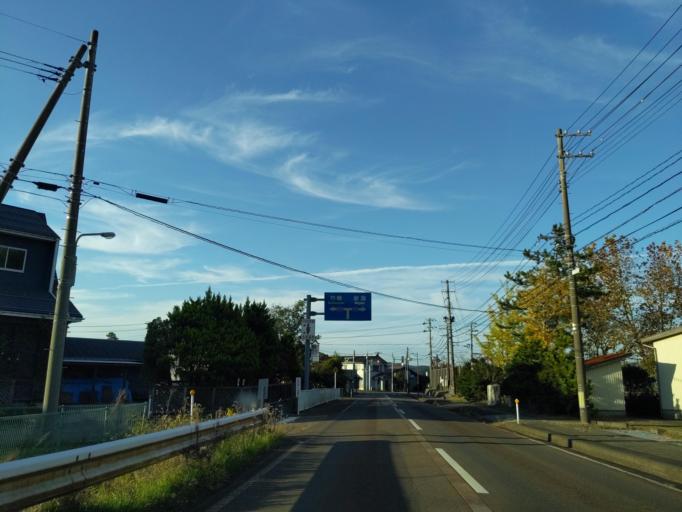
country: JP
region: Niigata
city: Yoshida-kasugacho
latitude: 37.5798
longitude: 138.7827
